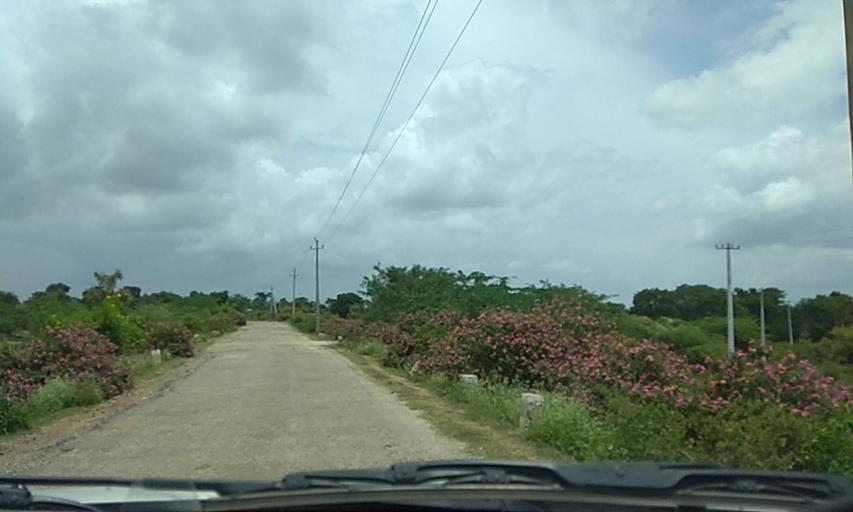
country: IN
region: Karnataka
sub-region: Chamrajnagar
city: Gundlupet
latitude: 11.8844
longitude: 76.6858
